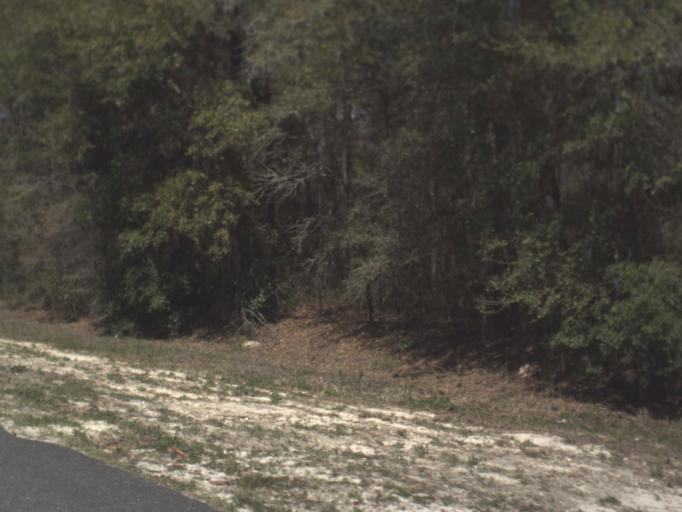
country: US
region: Florida
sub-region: Wakulla County
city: Crawfordville
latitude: 30.2724
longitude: -84.3767
